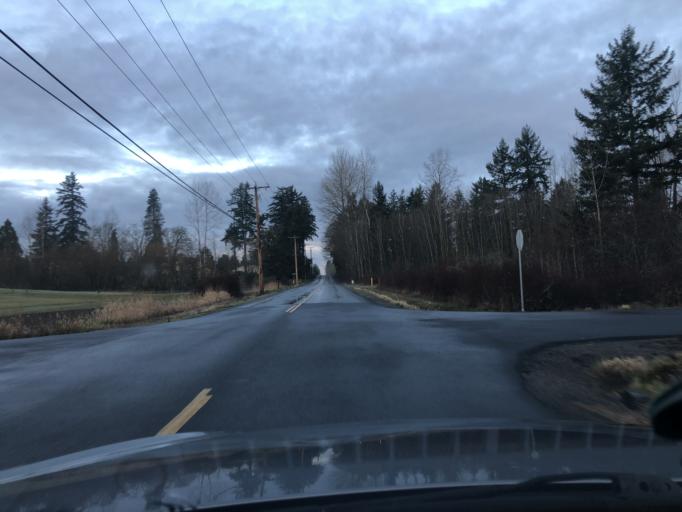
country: US
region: Washington
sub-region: Pierce County
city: North Puyallup
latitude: 47.2249
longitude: -122.2858
